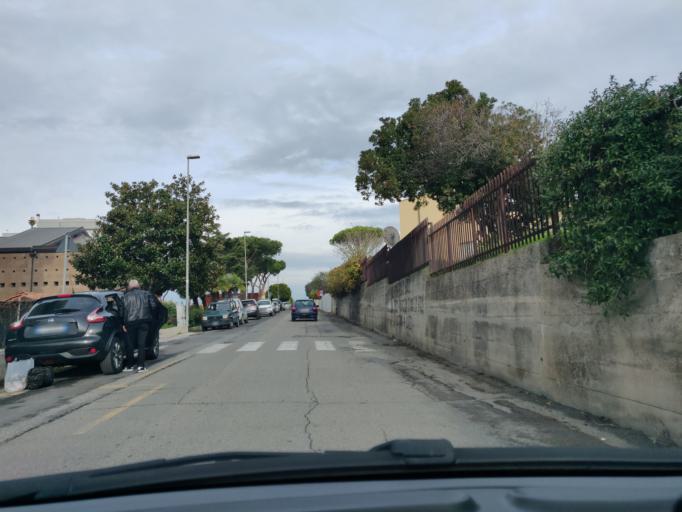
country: IT
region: Latium
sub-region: Citta metropolitana di Roma Capitale
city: Civitavecchia
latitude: 42.0968
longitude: 11.8147
